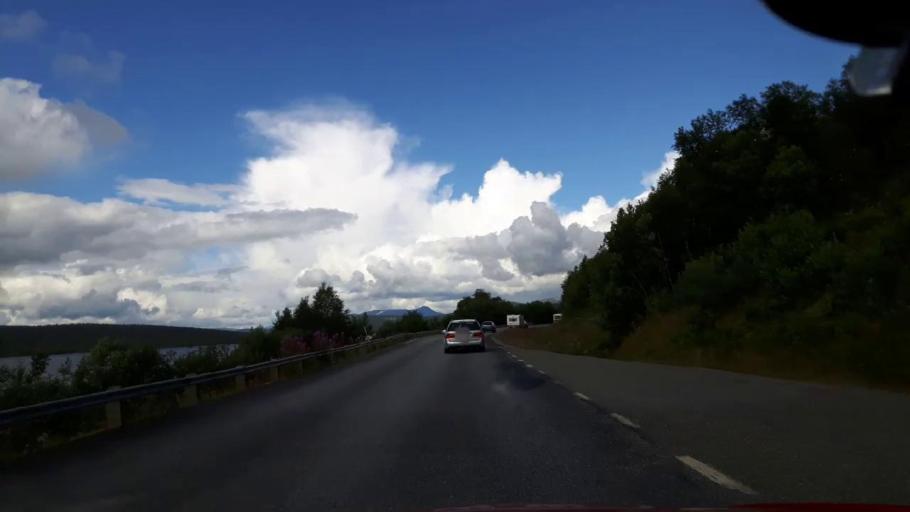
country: SE
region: Vaesterbotten
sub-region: Vilhelmina Kommun
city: Sjoberg
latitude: 65.0396
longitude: 15.1144
